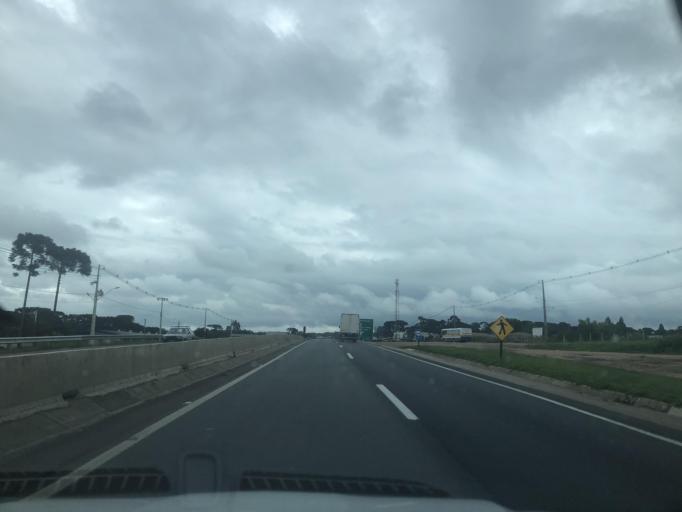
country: BR
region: Parana
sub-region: Araucaria
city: Araucaria
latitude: -25.6790
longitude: -49.3160
